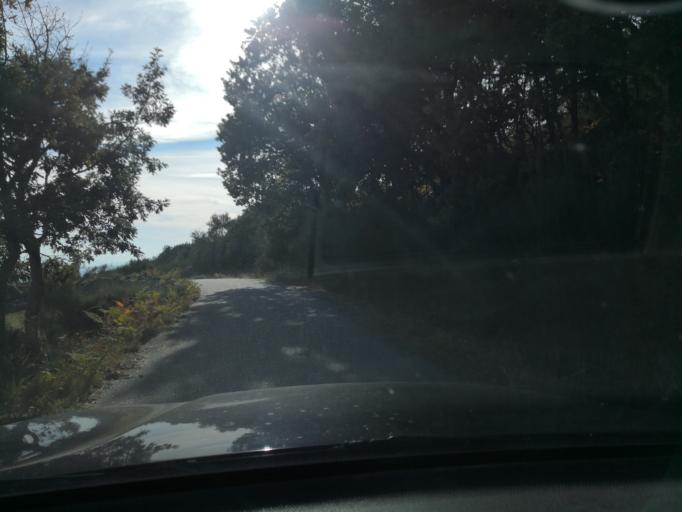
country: PT
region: Vila Real
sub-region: Vila Real
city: Vila Real
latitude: 41.3445
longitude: -7.7636
